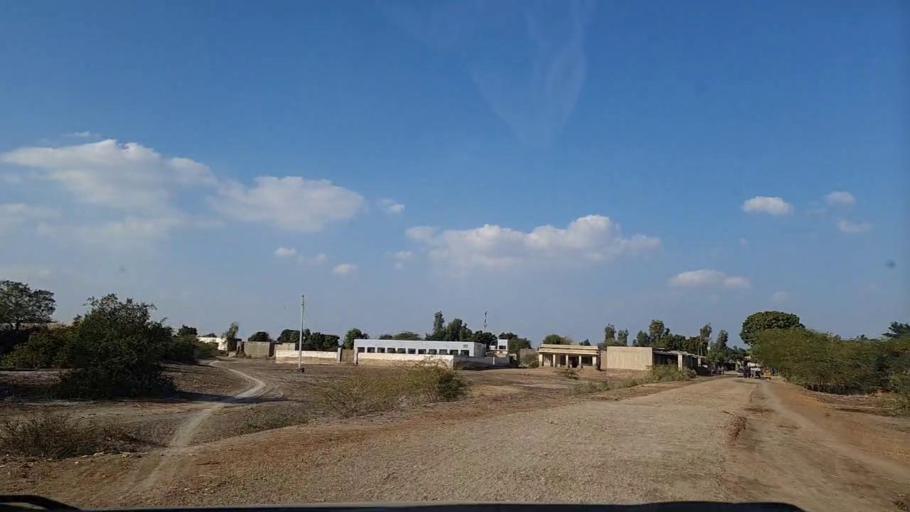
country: PK
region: Sindh
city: Pithoro
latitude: 25.6445
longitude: 69.3481
